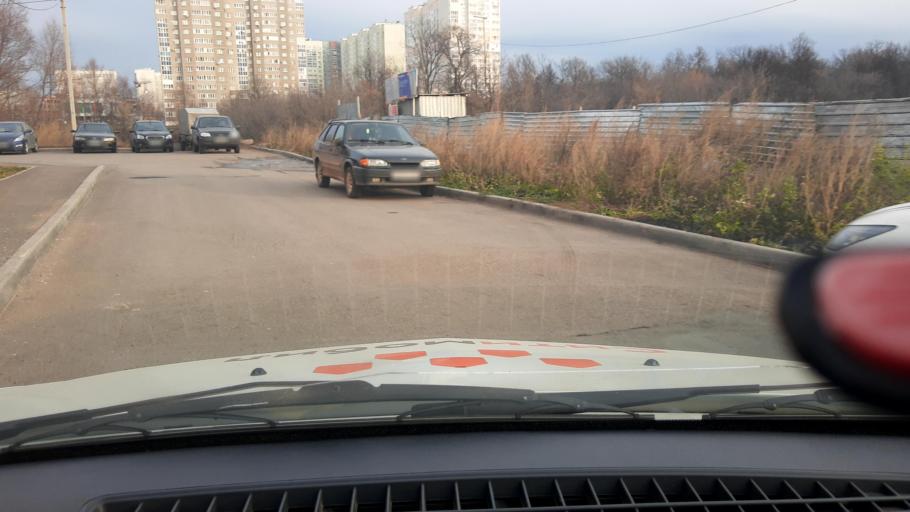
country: RU
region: Bashkortostan
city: Ufa
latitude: 54.7792
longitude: 56.1361
